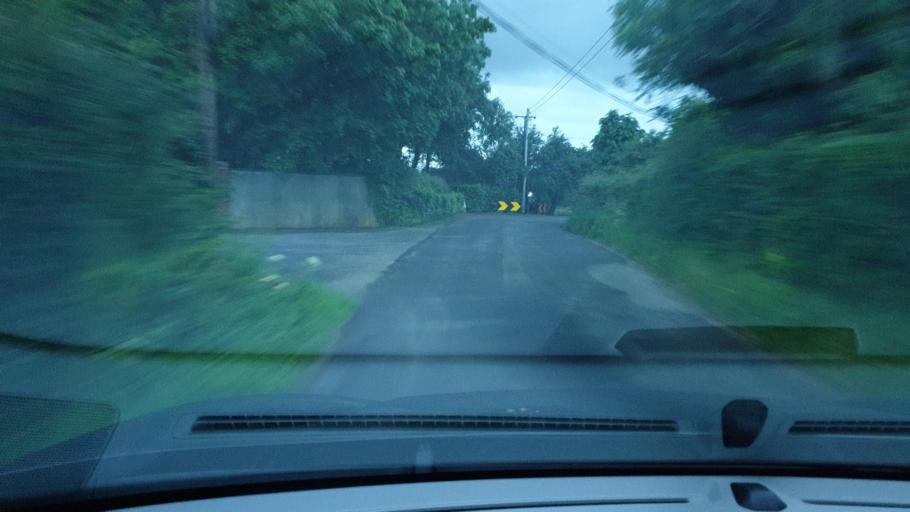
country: IE
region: Leinster
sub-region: An Mhi
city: Ashbourne
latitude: 53.5038
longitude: -6.3623
